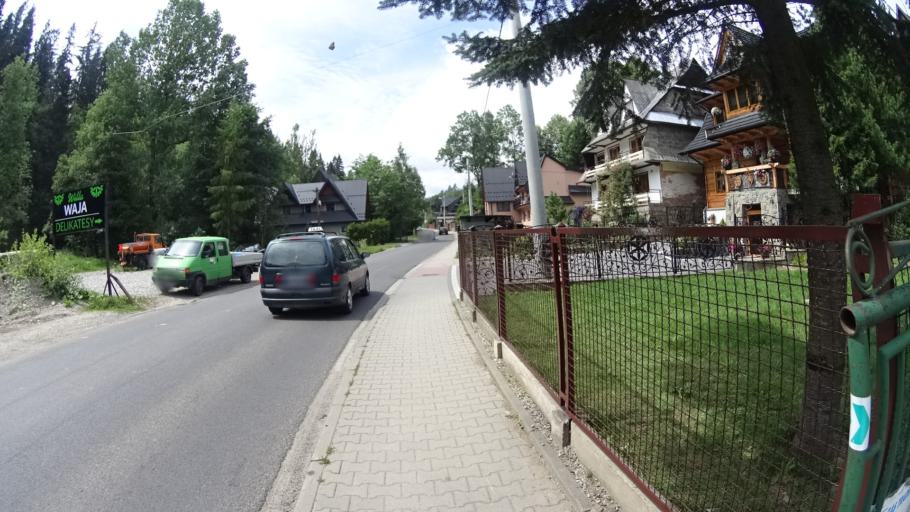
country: PL
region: Lesser Poland Voivodeship
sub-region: Powiat tatrzanski
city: Poronin
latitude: 49.3395
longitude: 19.9981
